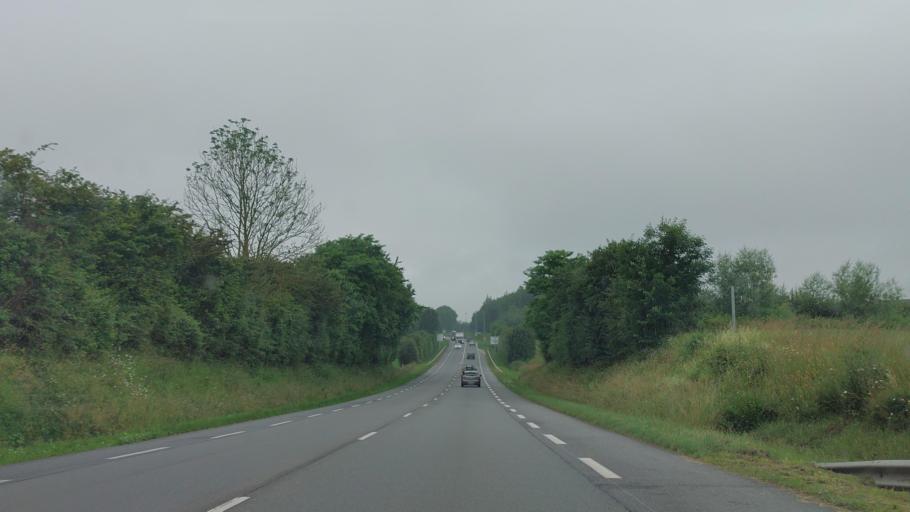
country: FR
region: Picardie
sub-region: Departement de la Somme
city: Friville-Escarbotin
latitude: 50.0734
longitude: 1.5490
